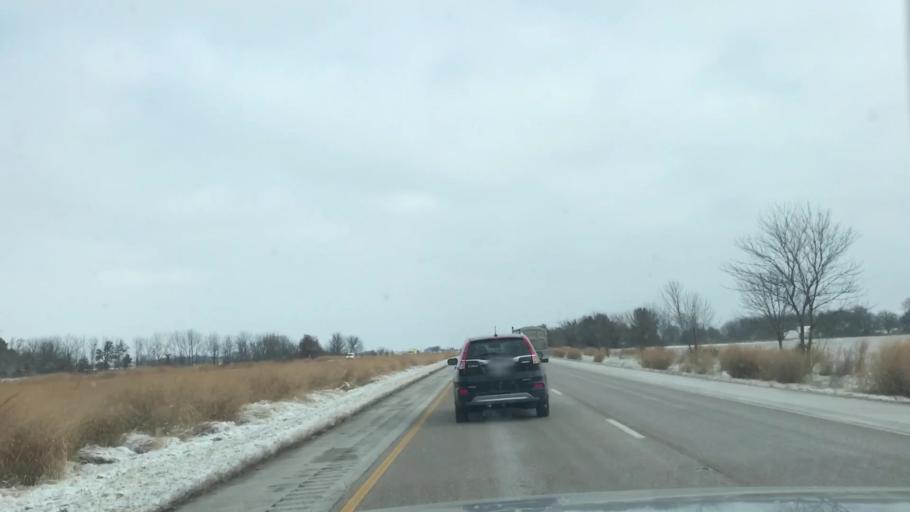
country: US
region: Illinois
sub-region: Macoupin County
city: Mount Olive
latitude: 39.1289
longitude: -89.7136
